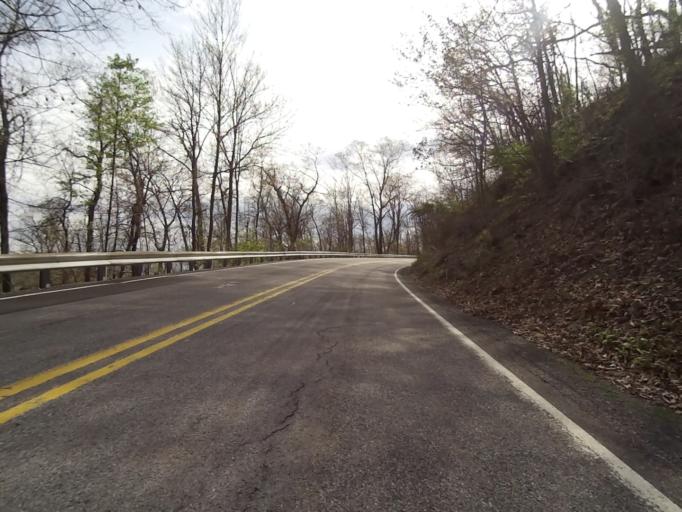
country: US
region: Pennsylvania
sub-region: Centre County
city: Stormstown
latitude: 40.8817
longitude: -78.0067
